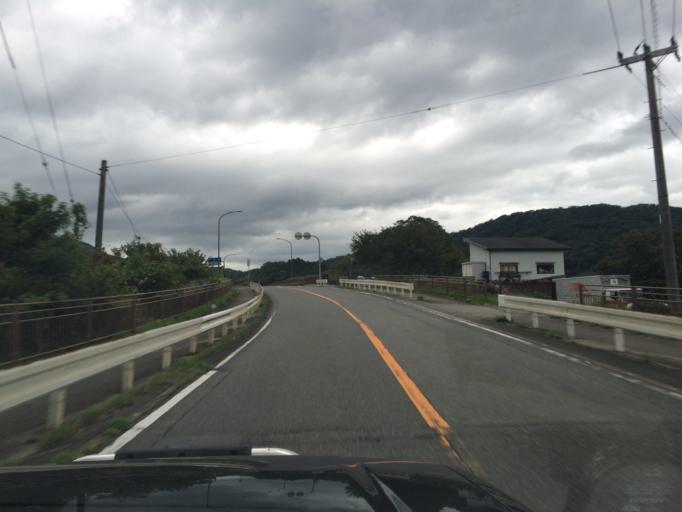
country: JP
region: Hyogo
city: Toyooka
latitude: 35.4259
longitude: 134.7915
